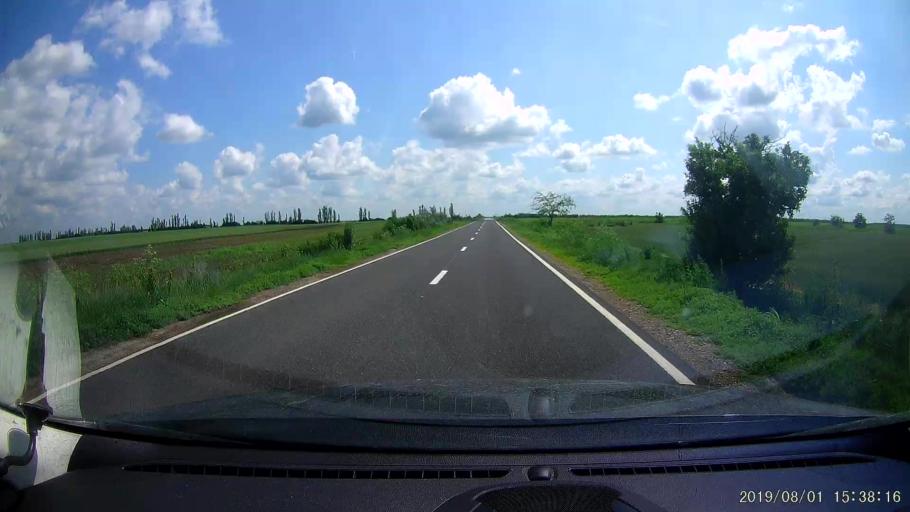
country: RO
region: Braila
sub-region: Comuna Insuratei
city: Insuratei
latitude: 44.8856
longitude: 27.5785
